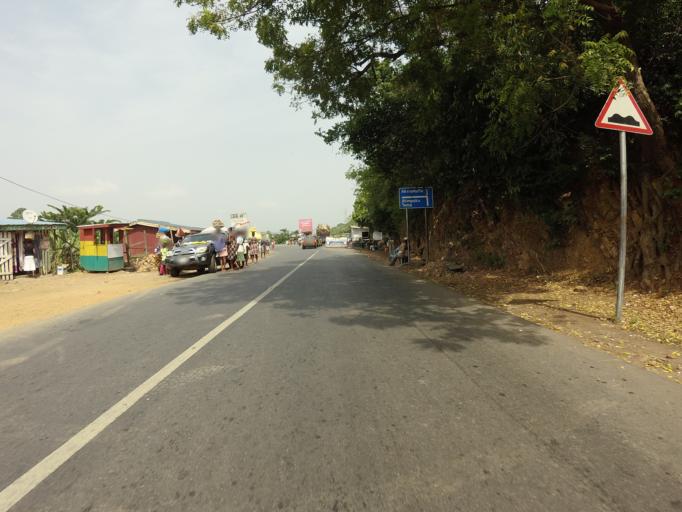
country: GH
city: Akropong
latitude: 6.2394
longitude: 0.0983
